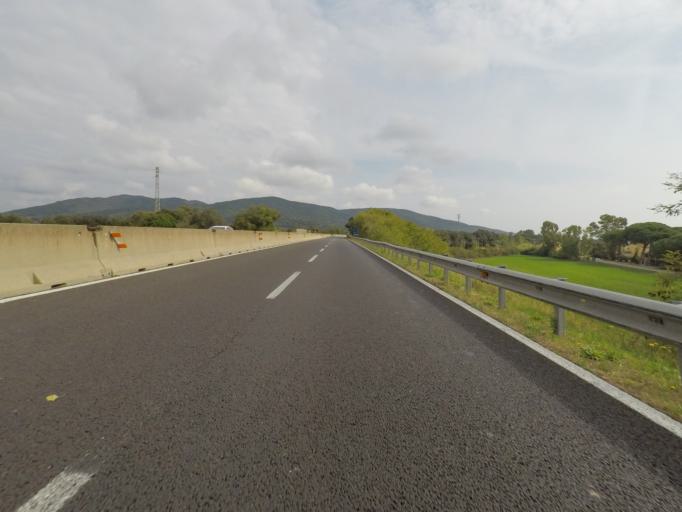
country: IT
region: Tuscany
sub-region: Provincia di Grosseto
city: Albinia
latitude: 42.4787
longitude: 11.2271
